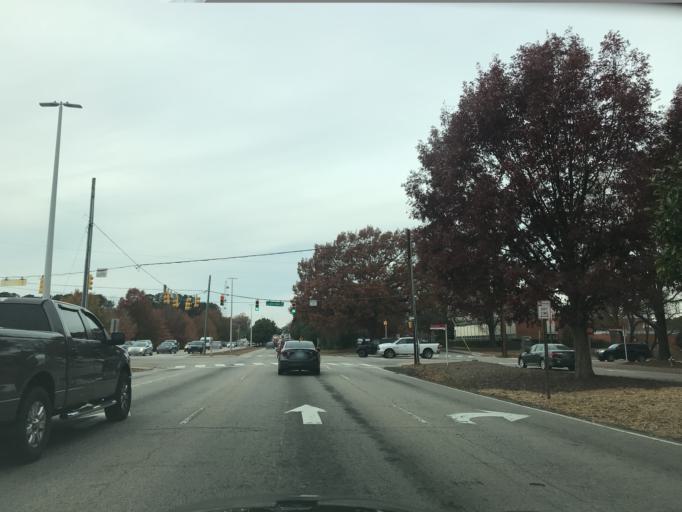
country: US
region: North Carolina
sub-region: Wake County
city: West Raleigh
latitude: 35.7820
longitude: -78.6782
